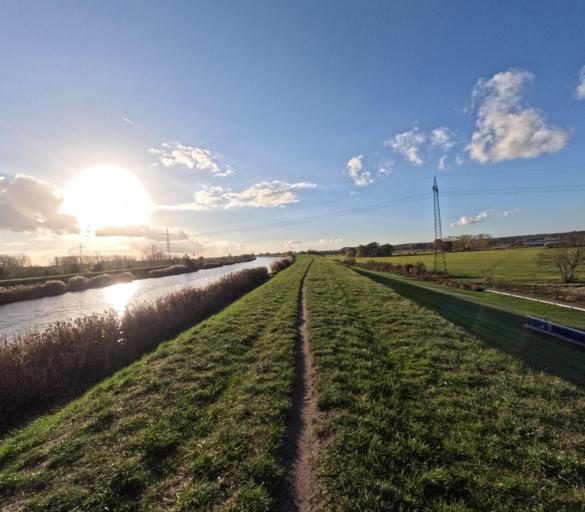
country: DE
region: Saxony-Anhalt
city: Gunthersdorf
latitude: 51.3585
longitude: 12.2073
